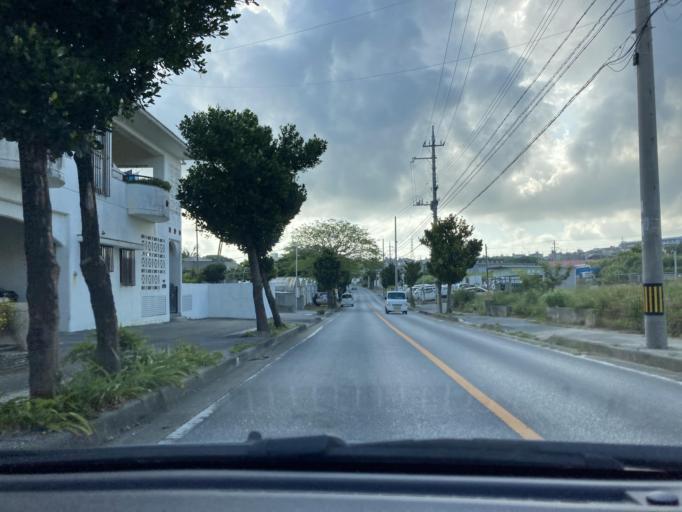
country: JP
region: Okinawa
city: Tomigusuku
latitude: 26.1756
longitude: 127.7196
